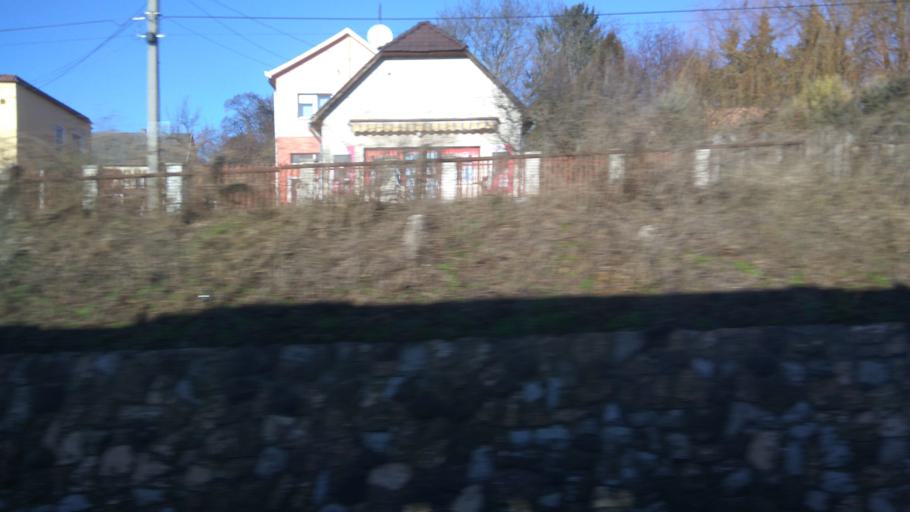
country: HU
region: Pest
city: Pecel
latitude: 47.4937
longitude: 19.3455
